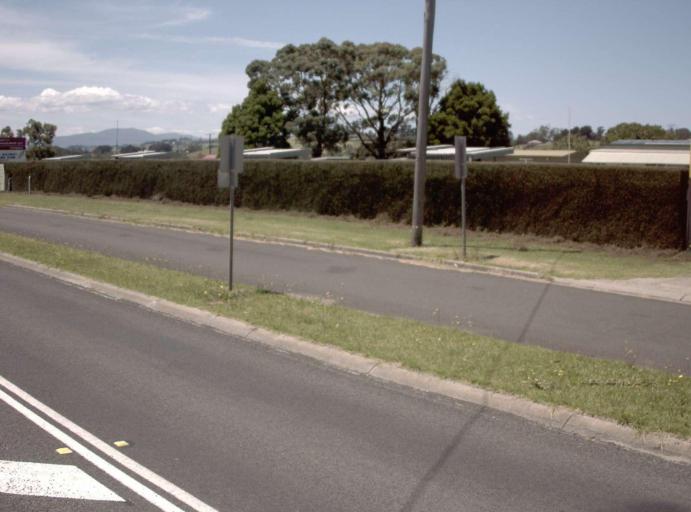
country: AU
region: Victoria
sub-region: Baw Baw
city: Warragul
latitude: -38.0241
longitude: 145.9542
